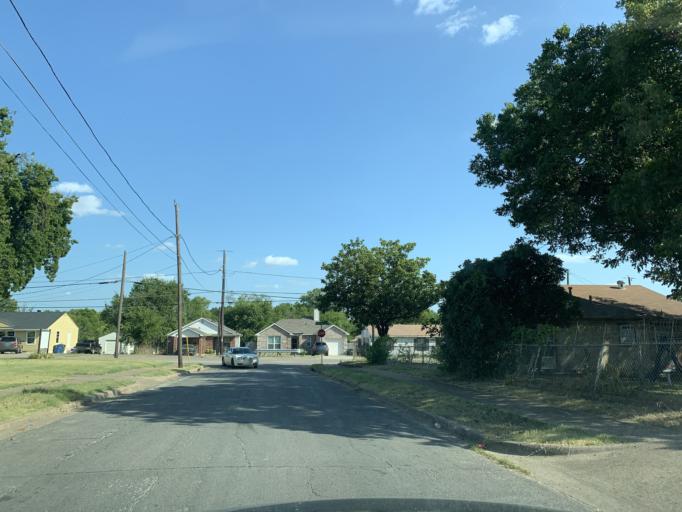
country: US
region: Texas
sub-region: Dallas County
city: Dallas
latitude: 32.7029
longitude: -96.7912
